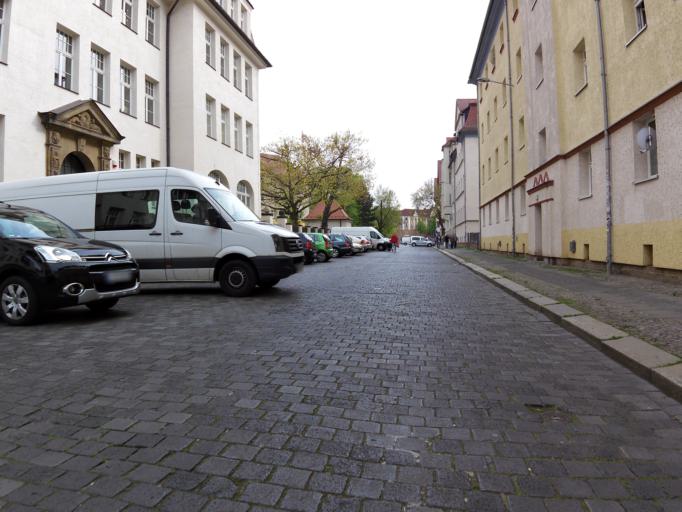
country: DE
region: Saxony
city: Leipzig
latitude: 51.3556
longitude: 12.4114
